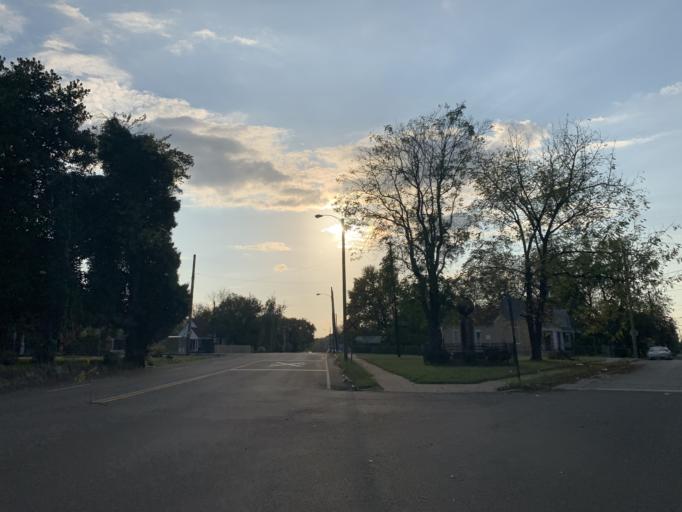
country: US
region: Kentucky
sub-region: Jefferson County
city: Shively
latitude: 38.2338
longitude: -85.7975
